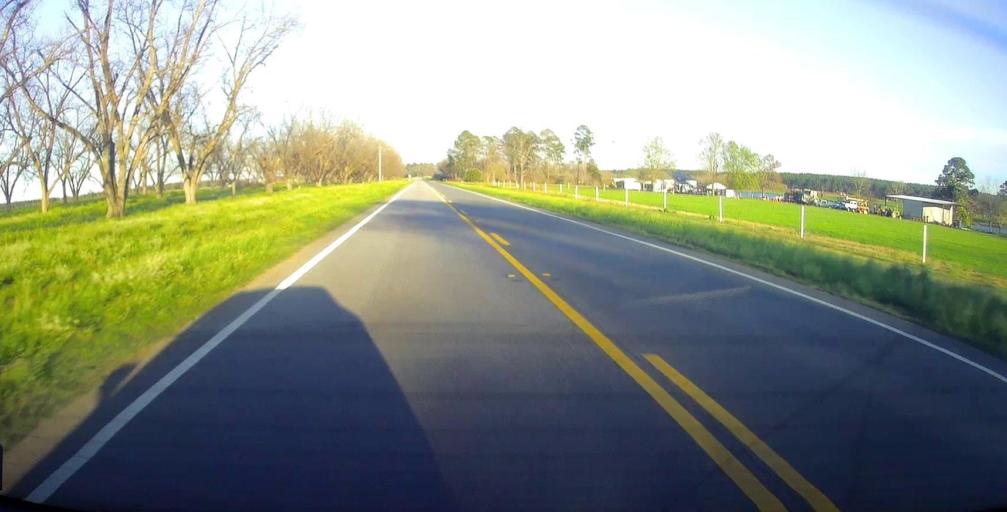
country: US
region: Georgia
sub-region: Wilcox County
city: Rochelle
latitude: 31.9609
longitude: -83.4110
